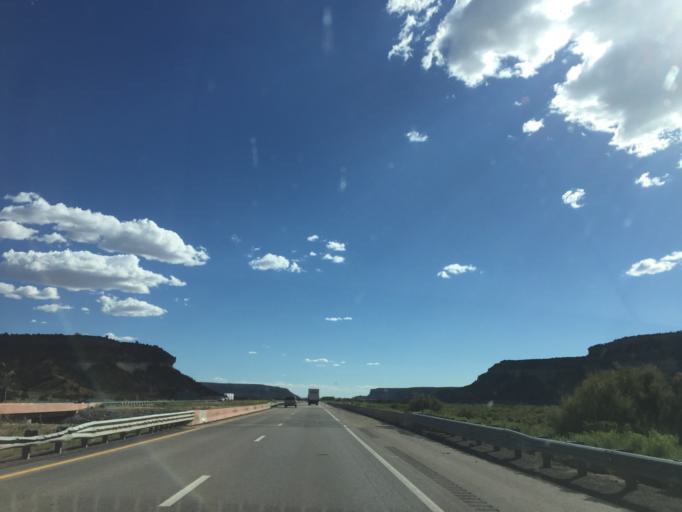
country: US
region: Arizona
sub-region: Apache County
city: Saint Michaels
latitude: 35.4168
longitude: -108.9930
